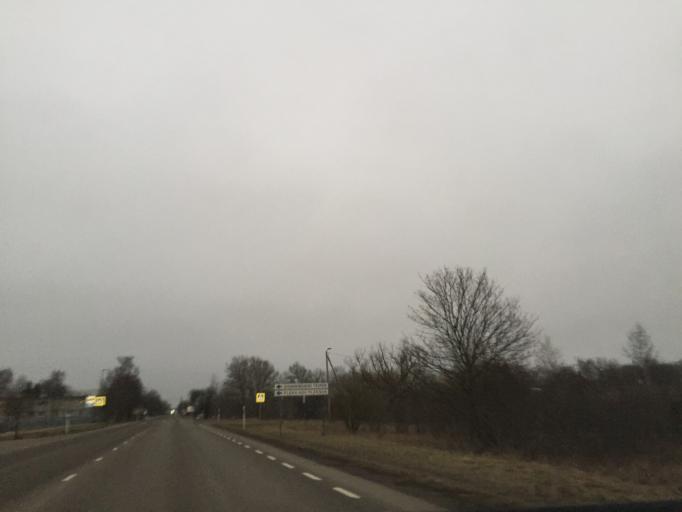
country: EE
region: Saare
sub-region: Kuressaare linn
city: Kuressaare
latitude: 58.2507
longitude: 22.5079
